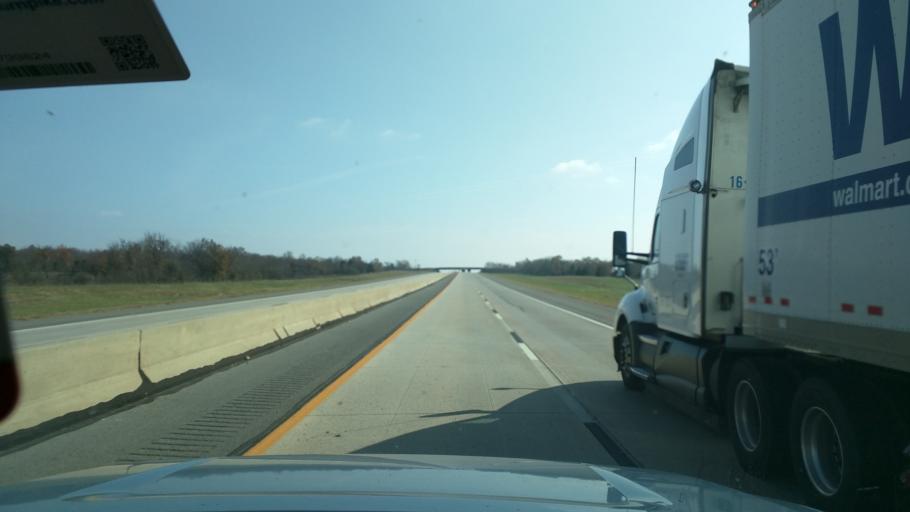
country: US
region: Oklahoma
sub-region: Wagoner County
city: Wagoner
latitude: 35.8755
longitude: -95.4747
